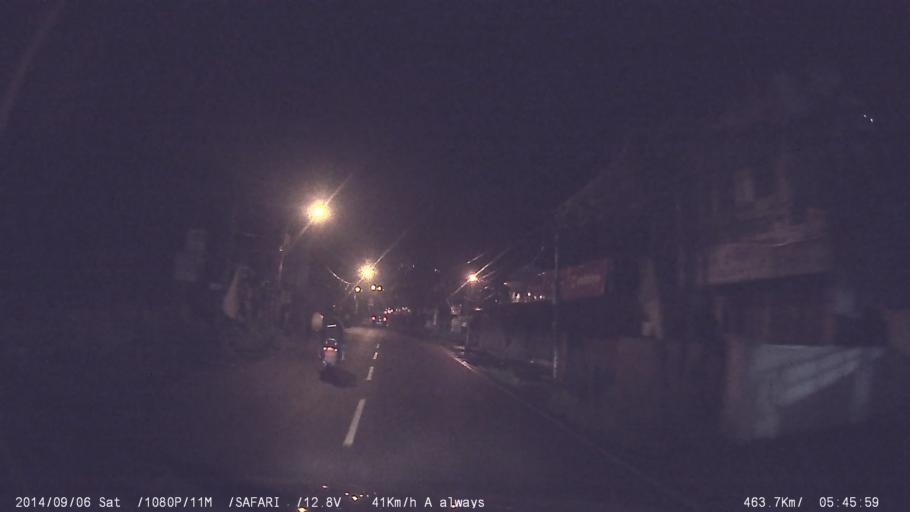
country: IN
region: Kerala
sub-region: Ernakulam
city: Cochin
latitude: 9.9588
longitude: 76.3254
